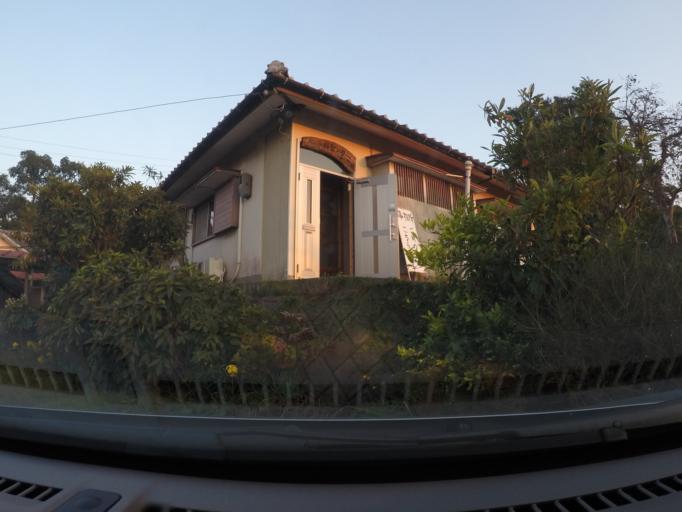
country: JP
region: Kumamoto
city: Minamata
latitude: 32.1845
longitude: 130.3878
